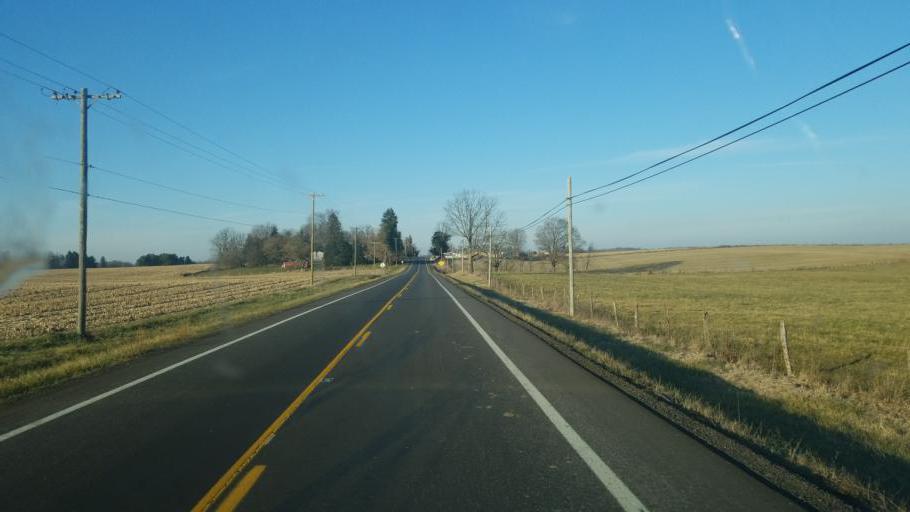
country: US
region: Ohio
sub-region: Richland County
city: Lexington
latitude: 40.6124
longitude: -82.6627
